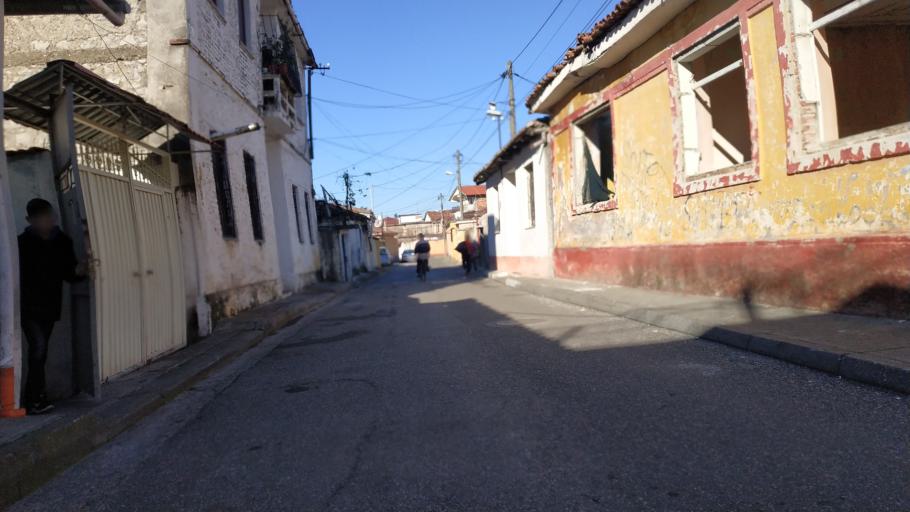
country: AL
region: Shkoder
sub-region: Rrethi i Shkodres
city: Shkoder
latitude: 42.0722
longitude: 19.5189
